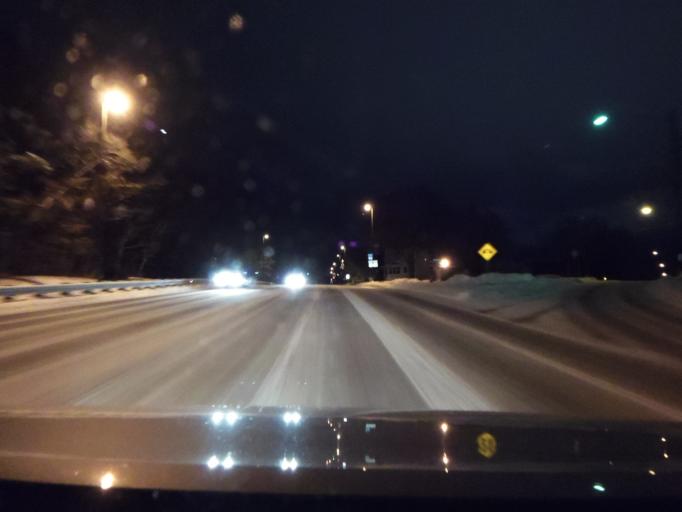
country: US
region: Wisconsin
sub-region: Dunn County
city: Menomonie
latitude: 44.8896
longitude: -91.9304
